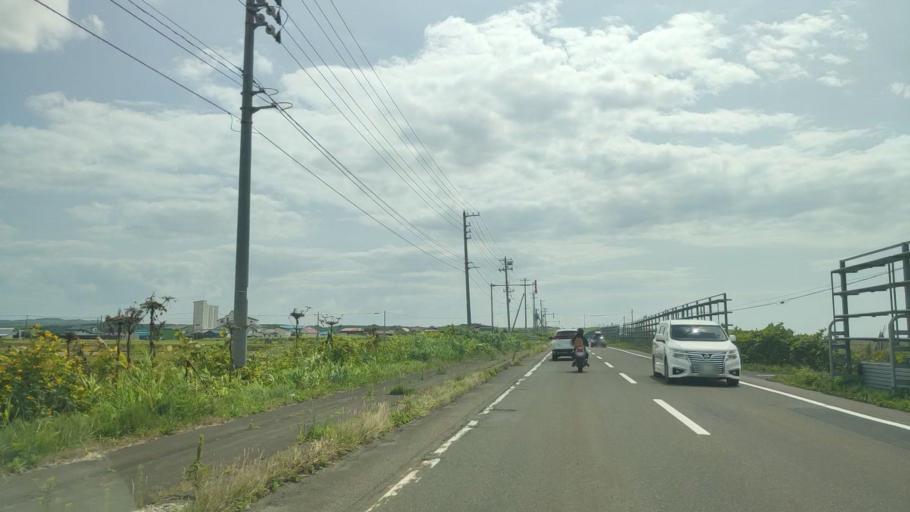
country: JP
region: Hokkaido
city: Rumoi
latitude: 44.4531
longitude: 141.7587
